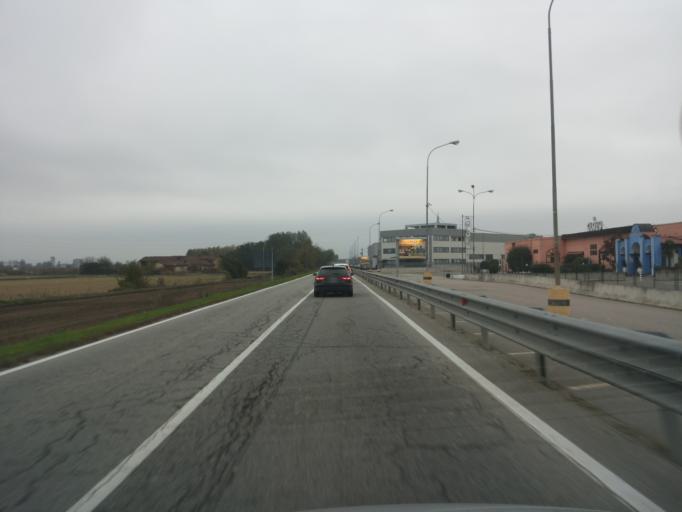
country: IT
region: Piedmont
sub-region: Provincia di Vercelli
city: Borgo Vercelli
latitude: 45.3412
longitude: 8.4521
